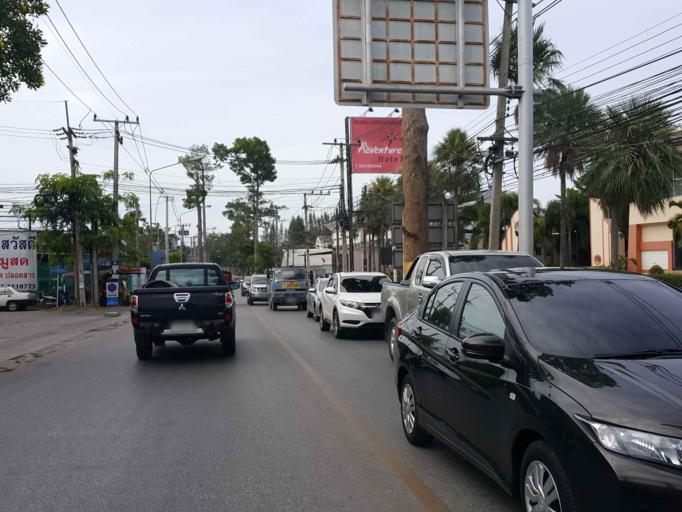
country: TH
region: Chiang Mai
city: Chiang Mai
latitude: 18.7575
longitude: 99.0075
